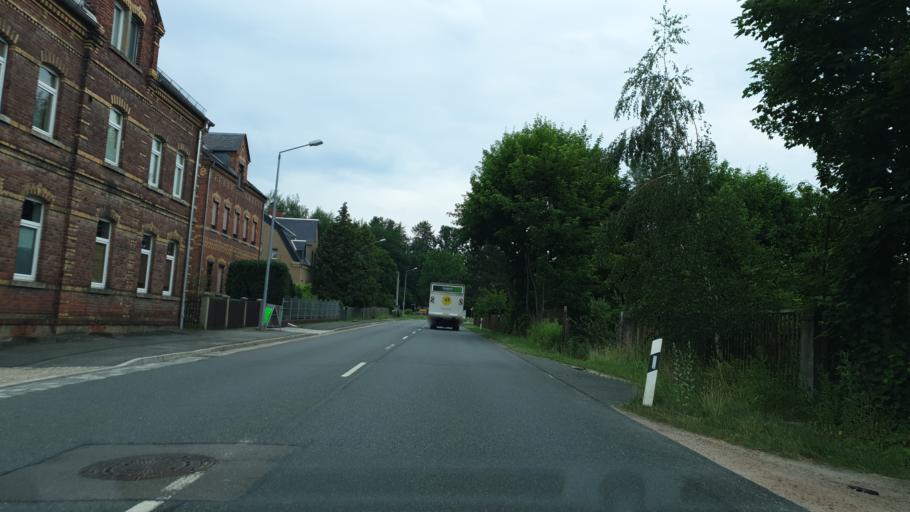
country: DE
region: Saxony
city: Lengenfeld
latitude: 50.5661
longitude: 12.3830
